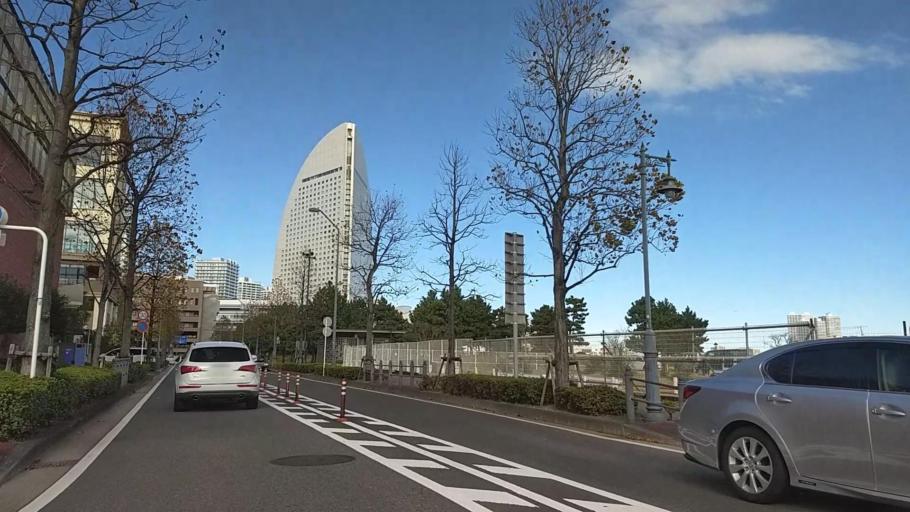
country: JP
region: Kanagawa
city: Yokohama
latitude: 35.4548
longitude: 139.6411
